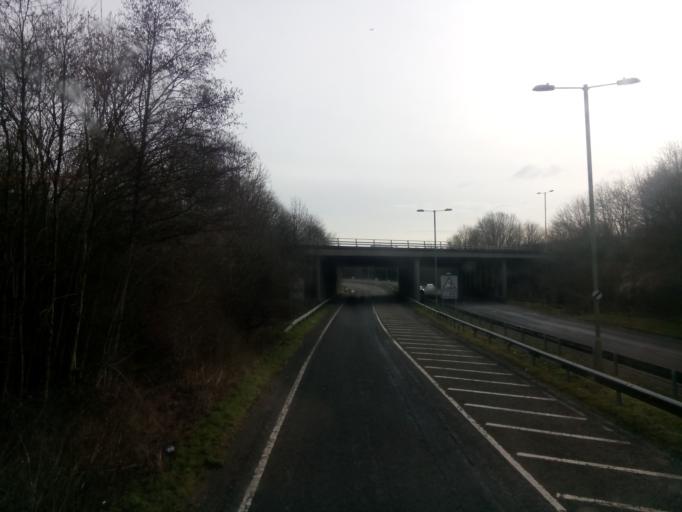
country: GB
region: England
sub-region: Hampshire
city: Basingstoke
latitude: 51.2676
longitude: -1.0703
